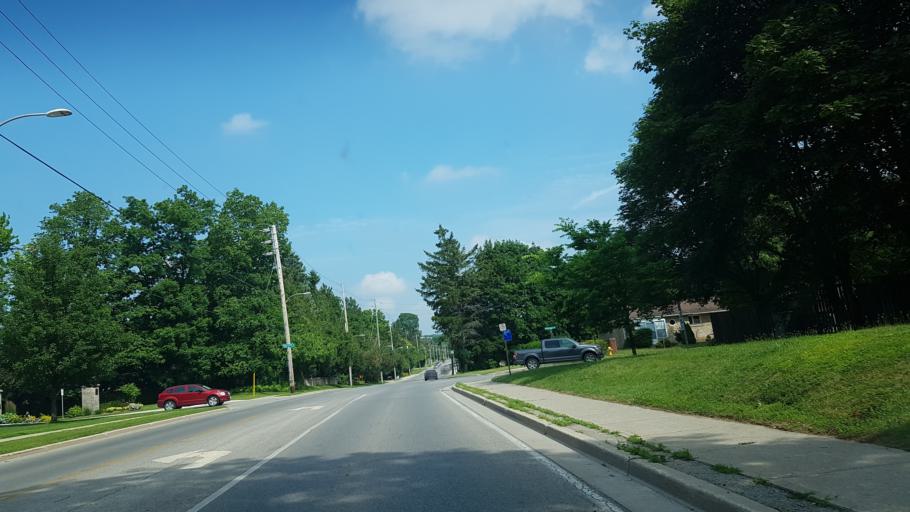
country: CA
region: Ontario
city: Delaware
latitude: 42.9634
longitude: -81.3447
